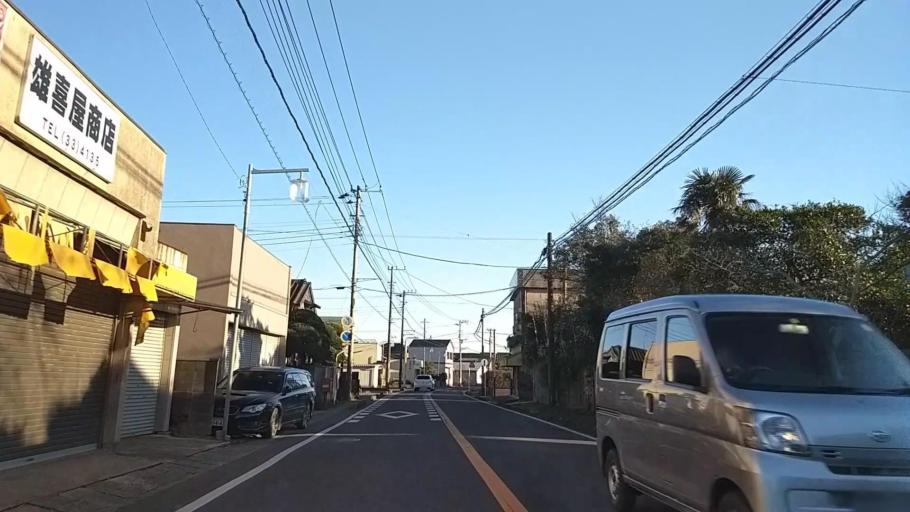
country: JP
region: Chiba
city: Hasaki
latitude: 35.7635
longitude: 140.7648
